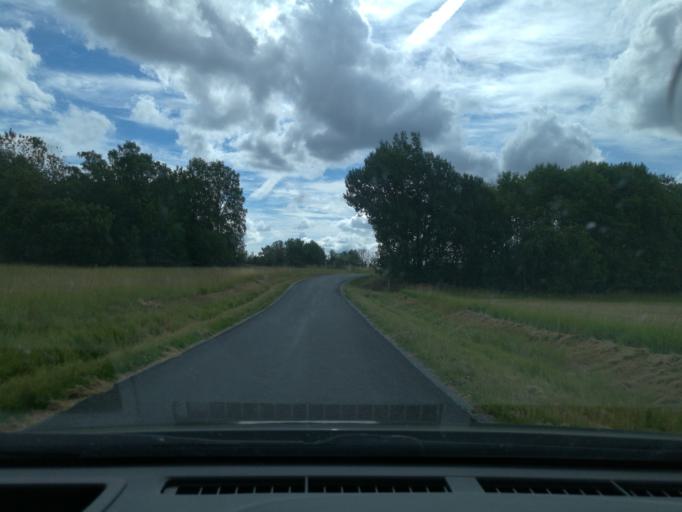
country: SE
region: Stockholm
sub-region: Sigtuna Kommun
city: Marsta
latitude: 59.6507
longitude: 17.8824
